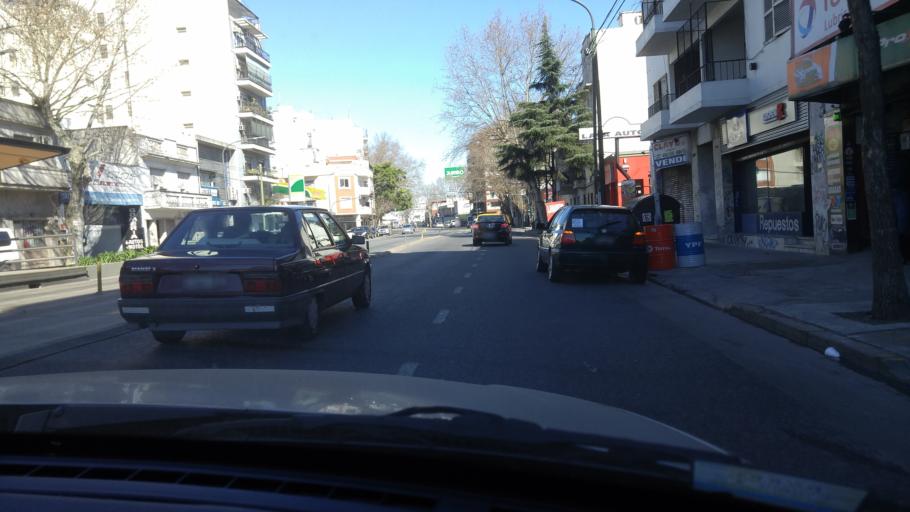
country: AR
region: Buenos Aires F.D.
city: Villa Santa Rita
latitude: -34.6076
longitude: -58.4631
